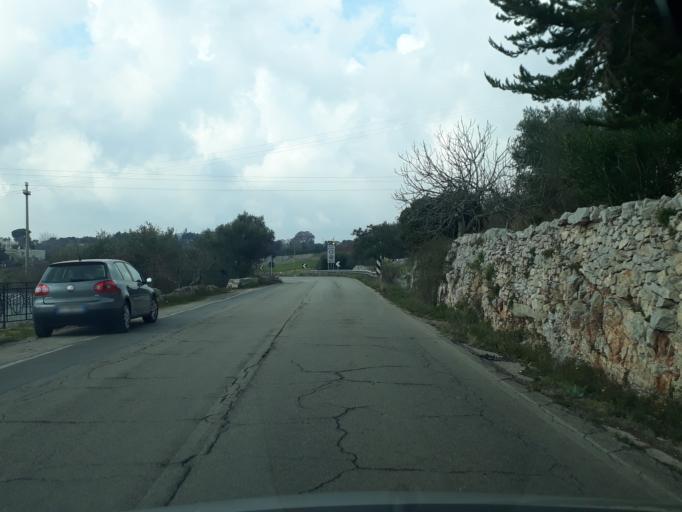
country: IT
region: Apulia
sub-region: Provincia di Brindisi
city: Cisternino
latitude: 40.7473
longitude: 17.4091
